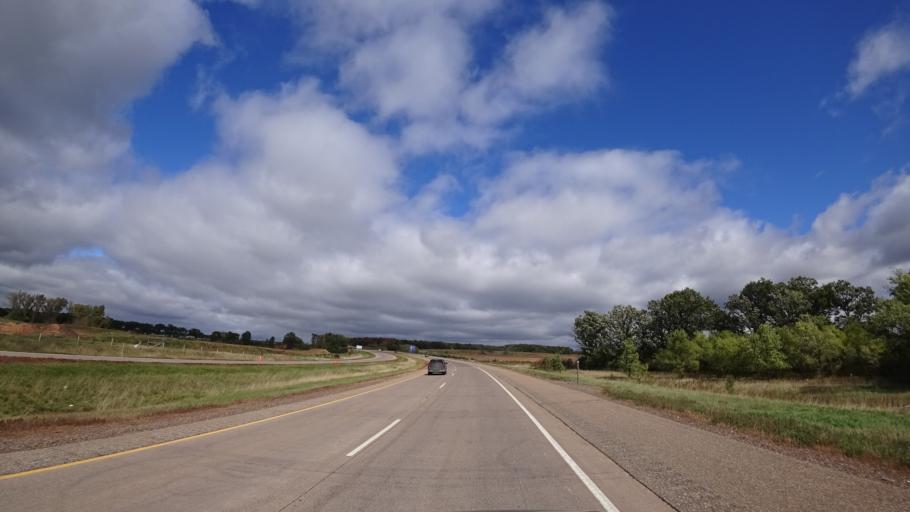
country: US
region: Wisconsin
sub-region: Chippewa County
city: Chippewa Falls
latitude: 44.9013
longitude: -91.3747
